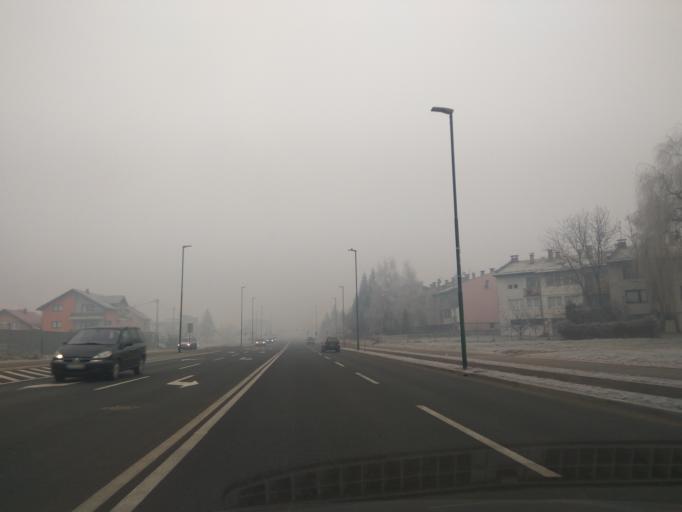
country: BA
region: Federation of Bosnia and Herzegovina
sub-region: Kanton Sarajevo
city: Sarajevo
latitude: 43.8292
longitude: 18.3348
